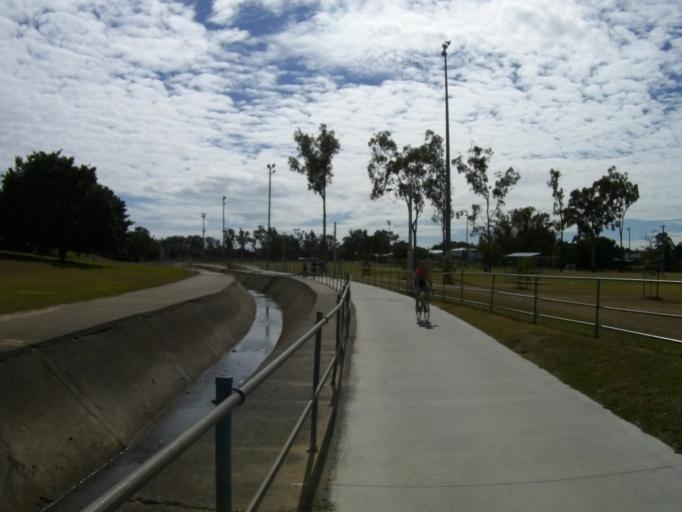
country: AU
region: Queensland
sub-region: Brisbane
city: Greenslopes
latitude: -27.5074
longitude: 153.0416
